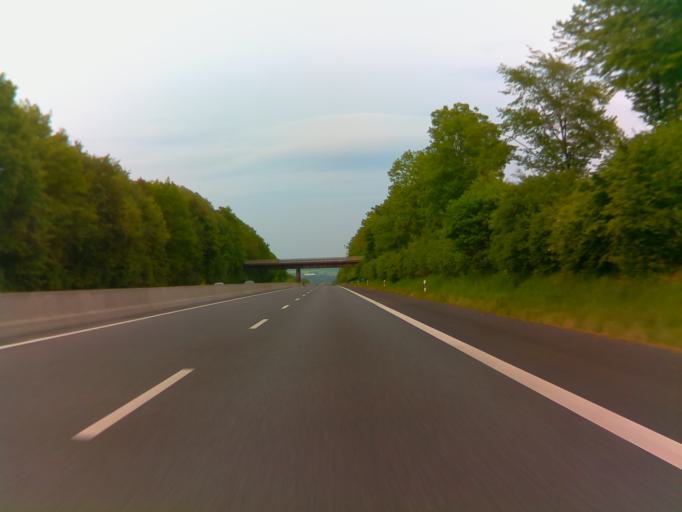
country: DE
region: Hesse
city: Fritzlar
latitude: 51.0876
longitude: 9.2643
